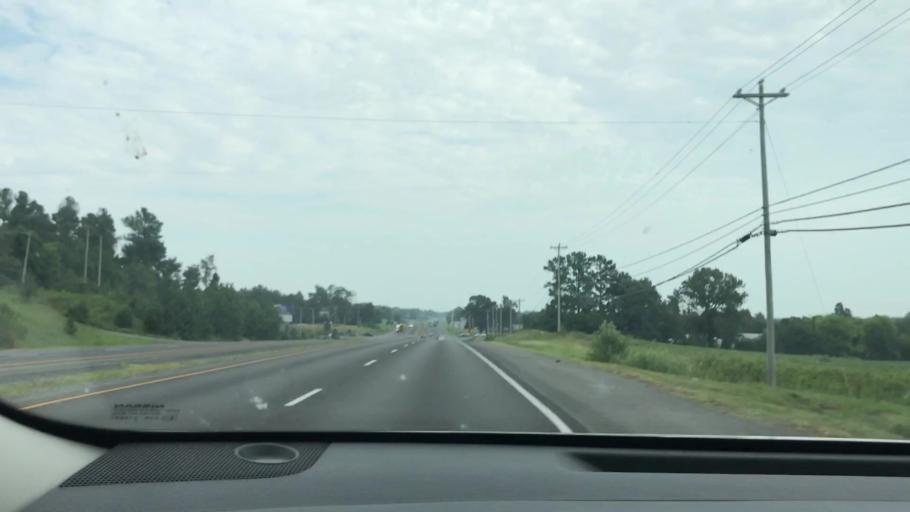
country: US
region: Kentucky
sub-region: Calloway County
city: Murray
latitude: 36.6485
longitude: -88.3075
